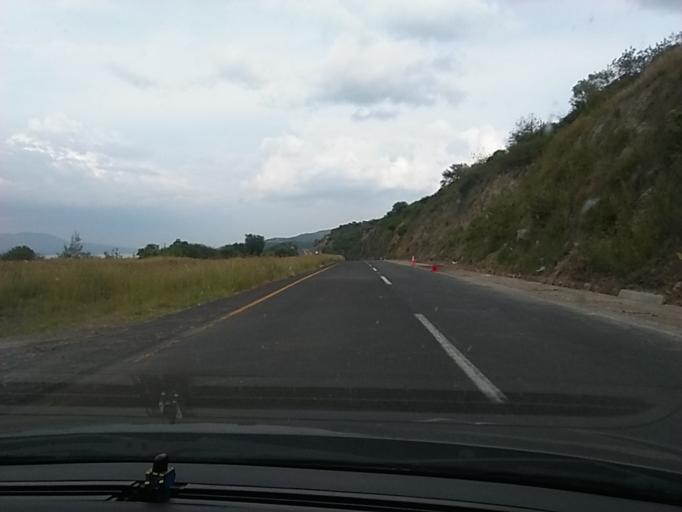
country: MX
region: Mexico
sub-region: Chapultepec
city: Chucandiro
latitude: 19.8831
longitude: -101.3426
